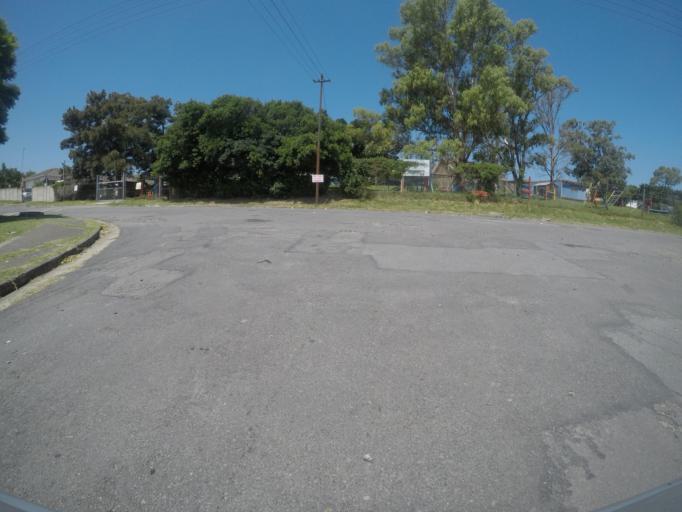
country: ZA
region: Eastern Cape
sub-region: Buffalo City Metropolitan Municipality
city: East London
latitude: -32.9736
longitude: 27.8668
